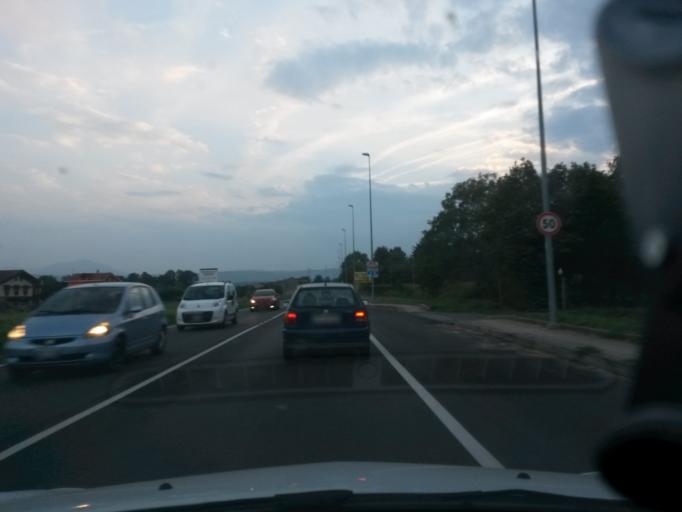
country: IT
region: Piedmont
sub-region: Provincia di Torino
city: Caselette
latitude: 45.1005
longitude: 7.4718
